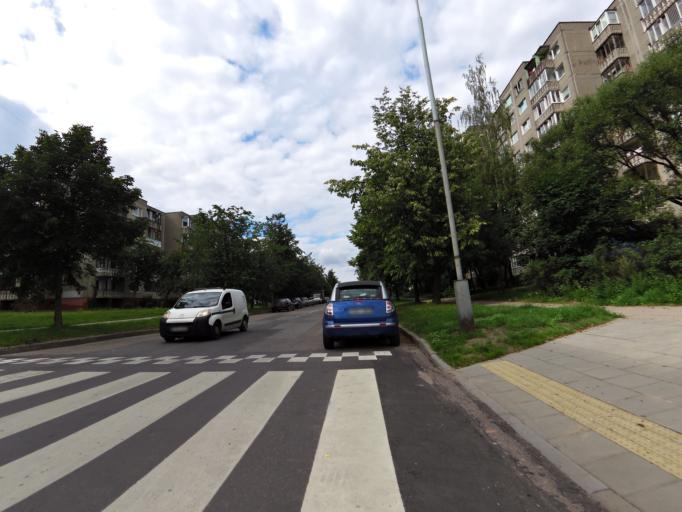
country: LT
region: Vilnius County
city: Seskine
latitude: 54.7174
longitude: 25.2375
